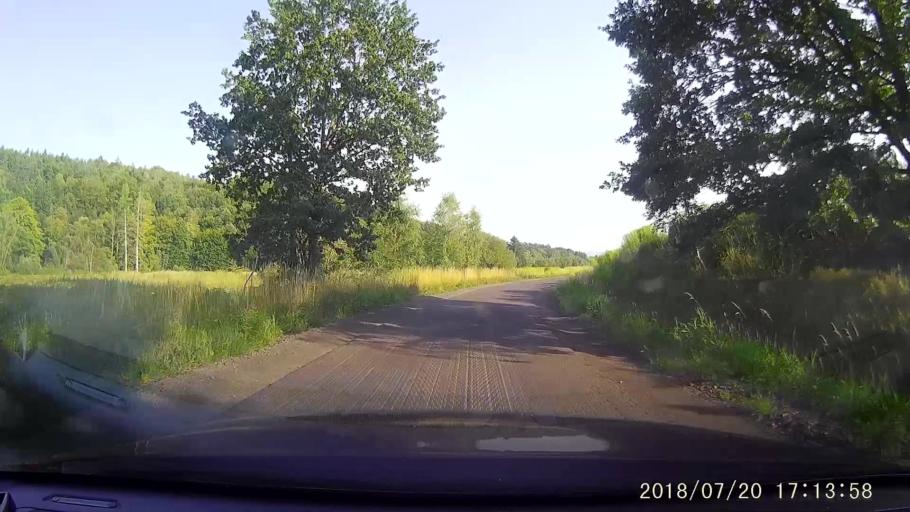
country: PL
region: Lower Silesian Voivodeship
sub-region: Powiat lubanski
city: Lesna
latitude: 51.0123
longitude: 15.2785
